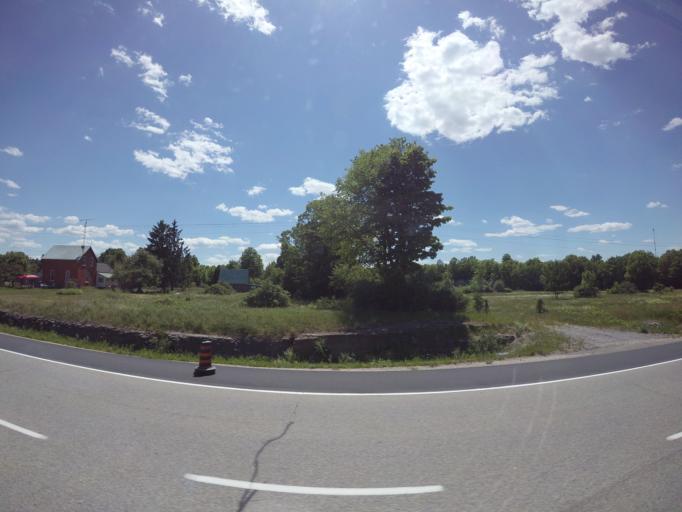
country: CA
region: Ontario
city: Carleton Place
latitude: 45.1312
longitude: -76.1715
